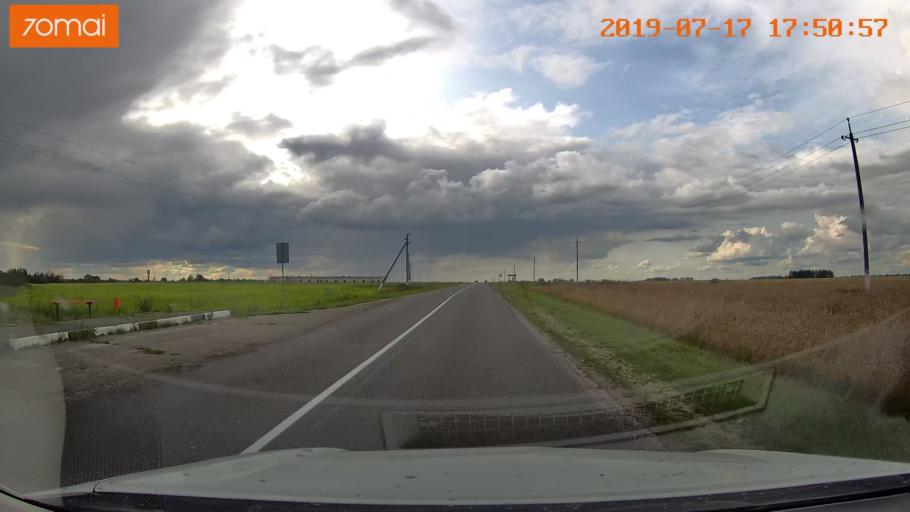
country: BY
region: Mogilev
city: Hlusha
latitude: 53.1466
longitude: 28.7947
